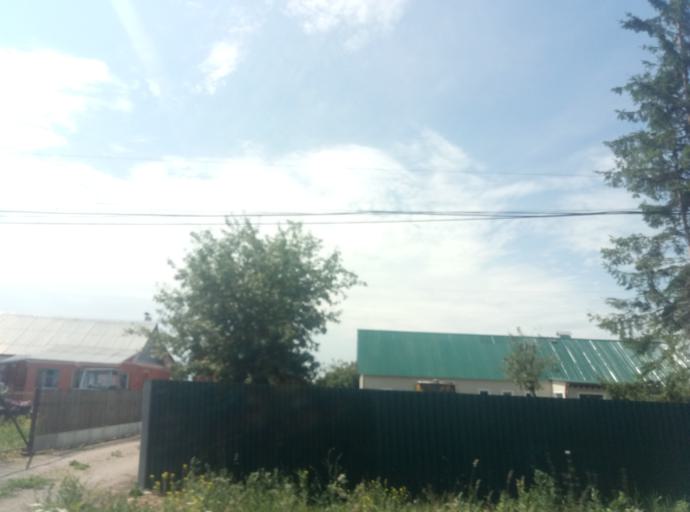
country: RU
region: Tula
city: Dubovka
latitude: 53.9031
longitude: 38.0308
